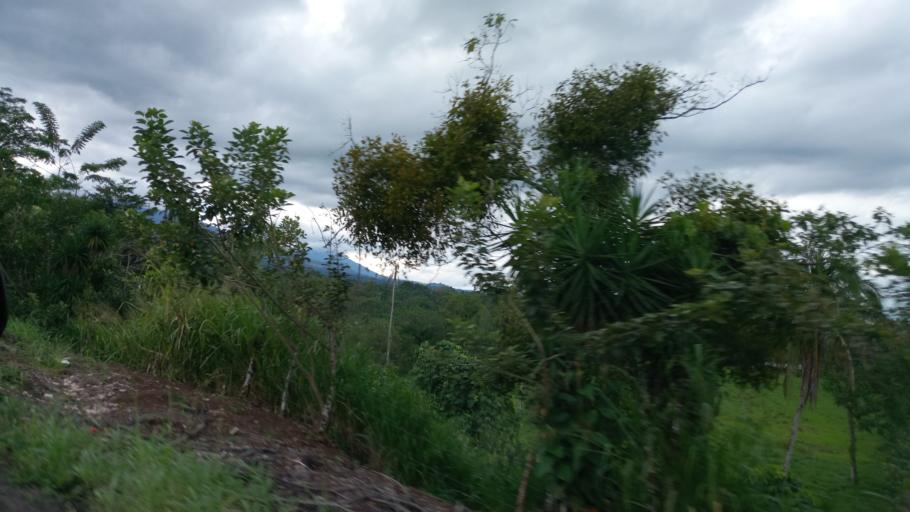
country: CR
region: Alajuela
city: Pocosol
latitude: 10.3740
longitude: -84.5620
